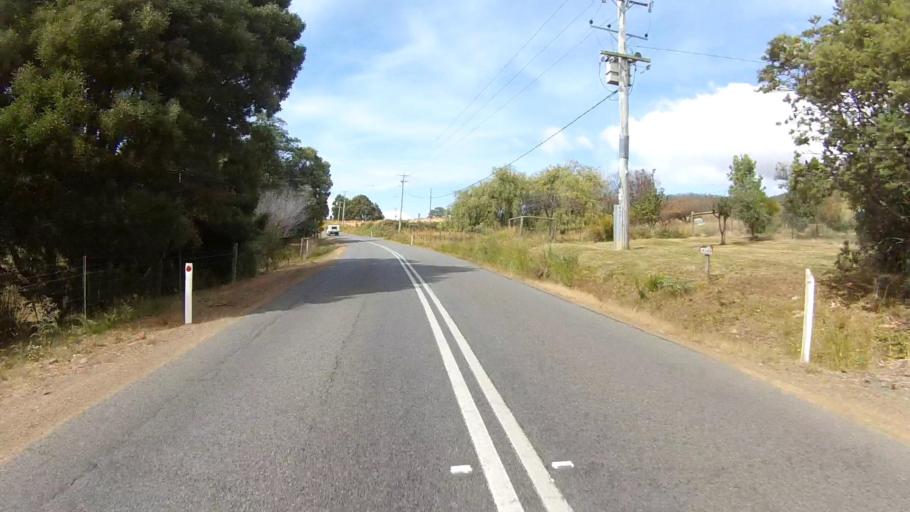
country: AU
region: Tasmania
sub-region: Kingborough
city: Kettering
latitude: -43.2096
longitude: 147.2558
